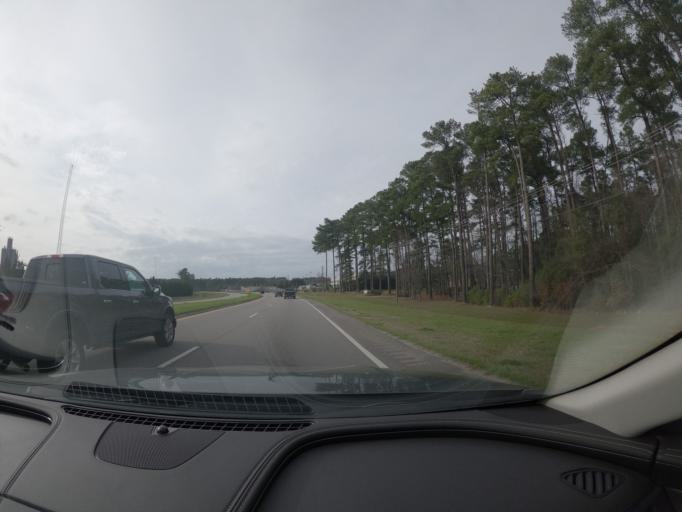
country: US
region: Georgia
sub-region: Columbia County
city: Martinez
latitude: 33.5246
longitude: -82.0383
